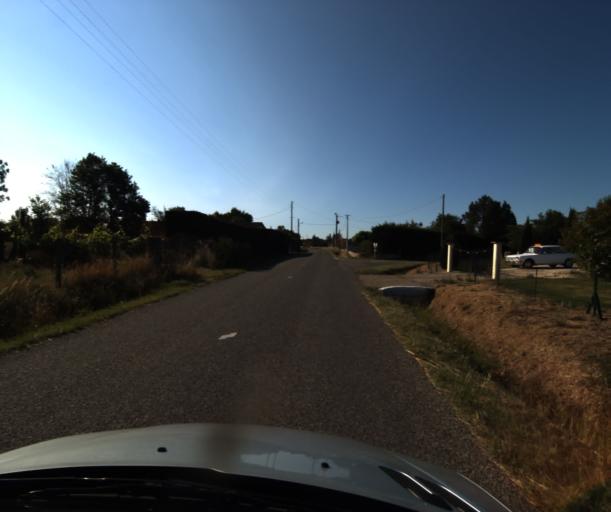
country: FR
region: Midi-Pyrenees
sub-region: Departement du Tarn-et-Garonne
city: Lafrancaise
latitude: 44.0740
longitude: 1.1951
